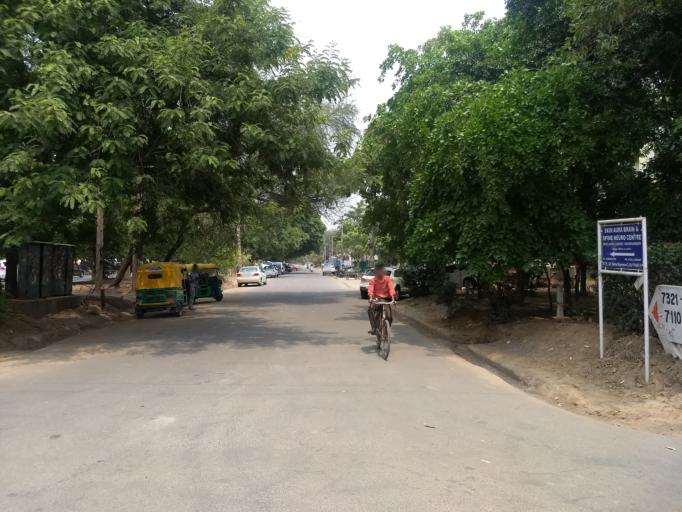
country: IN
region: Haryana
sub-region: Gurgaon
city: Gurgaon
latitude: 28.4615
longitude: 77.0871
